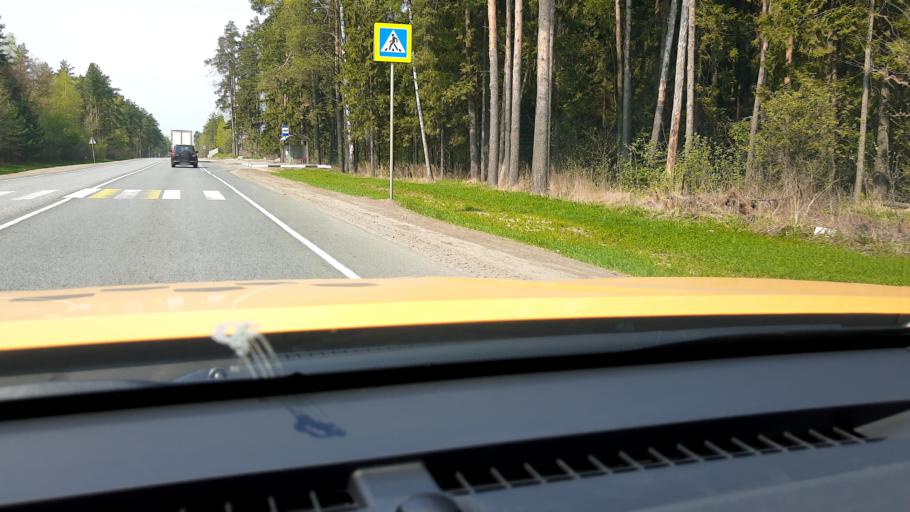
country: RU
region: Moskovskaya
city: Chernogolovka
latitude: 55.9936
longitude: 38.3240
